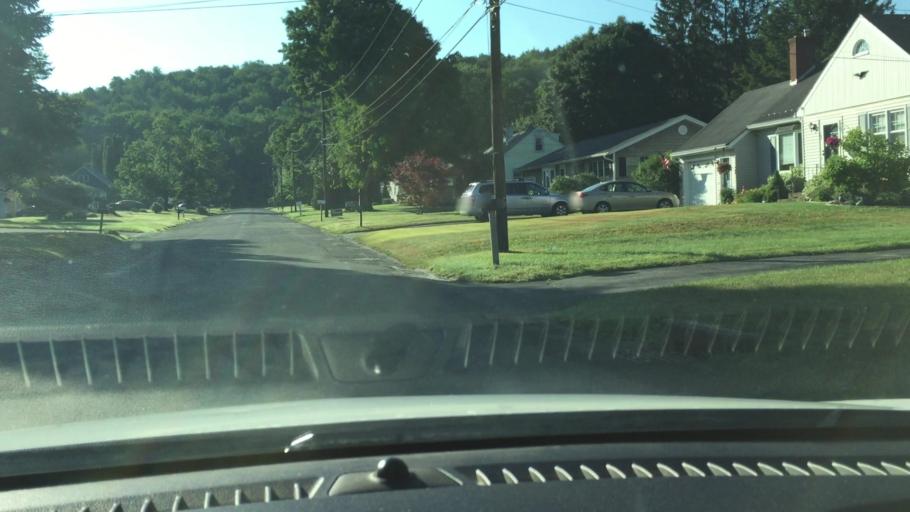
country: US
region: Massachusetts
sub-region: Berkshire County
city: Pittsfield
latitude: 42.4180
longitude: -73.2303
